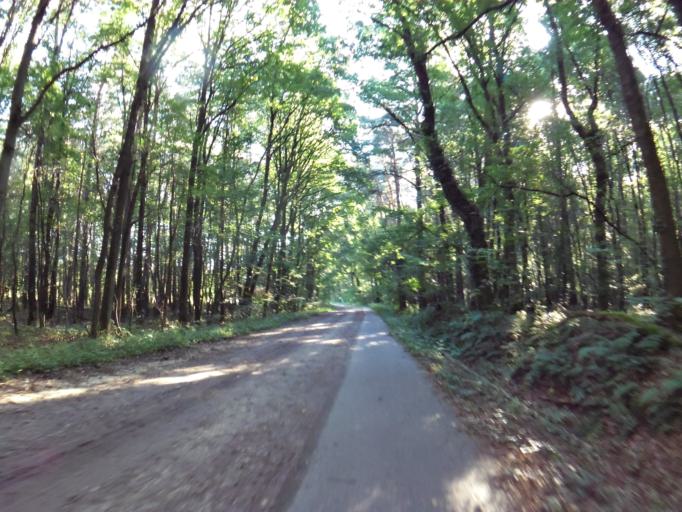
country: DE
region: North Rhine-Westphalia
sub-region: Regierungsbezirk Koln
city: Gangelt
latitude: 50.9759
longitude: 6.0046
